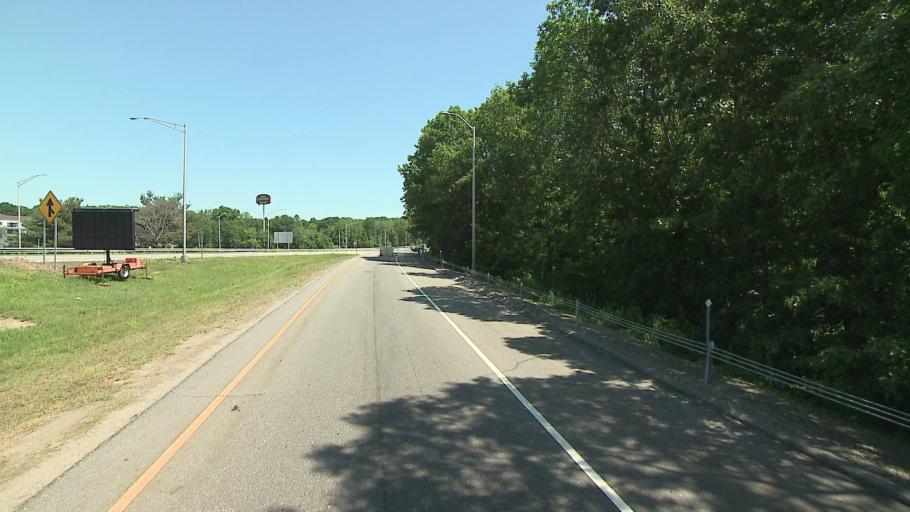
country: US
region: Connecticut
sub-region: New London County
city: Norwich
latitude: 41.5543
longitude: -72.1050
